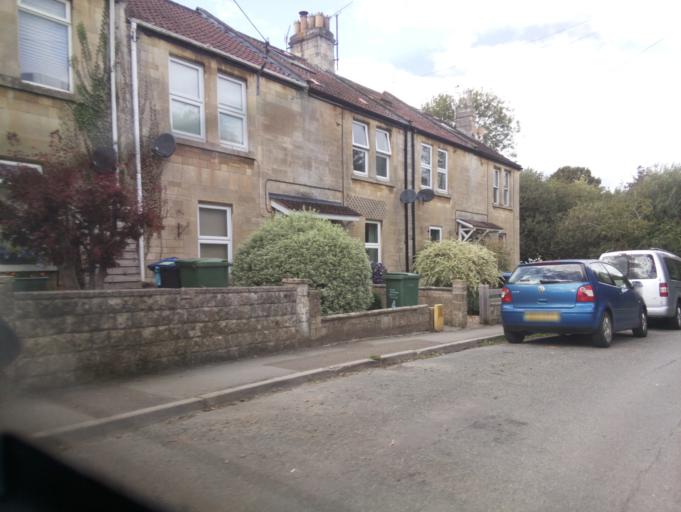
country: GB
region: England
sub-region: Wiltshire
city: Box
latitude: 51.4178
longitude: -2.2523
